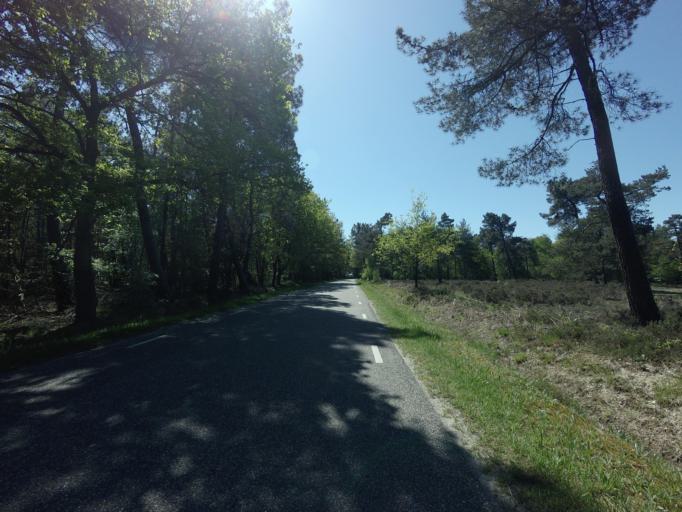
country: BE
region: Flanders
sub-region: Provincie Antwerpen
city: Essen
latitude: 51.4987
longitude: 4.4945
